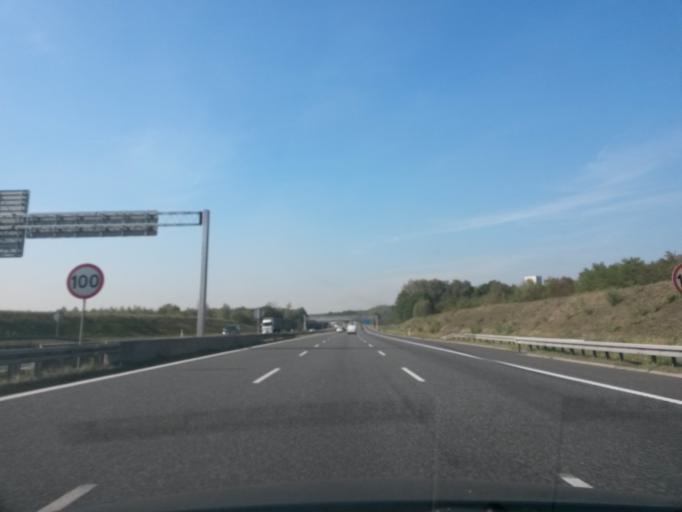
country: PL
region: Silesian Voivodeship
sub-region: Powiat gliwicki
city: Paniowki
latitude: 50.2642
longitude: 18.7825
